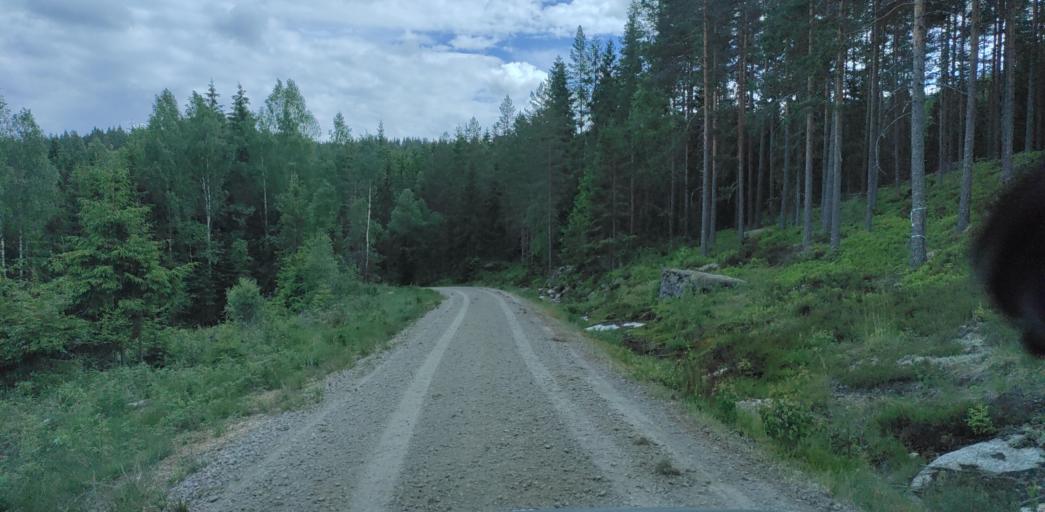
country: SE
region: Vaermland
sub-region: Munkfors Kommun
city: Munkfors
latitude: 59.9663
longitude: 13.4137
